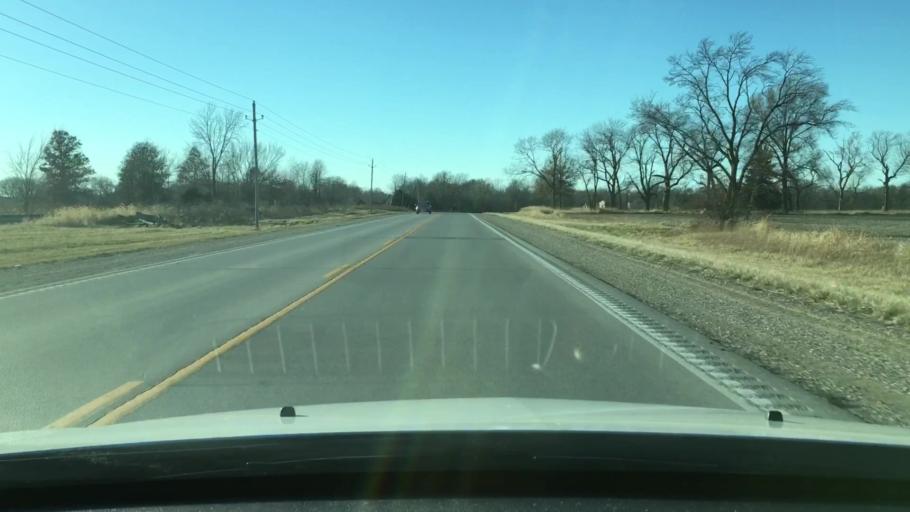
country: US
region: Missouri
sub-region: Audrain County
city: Mexico
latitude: 39.1886
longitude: -91.9744
